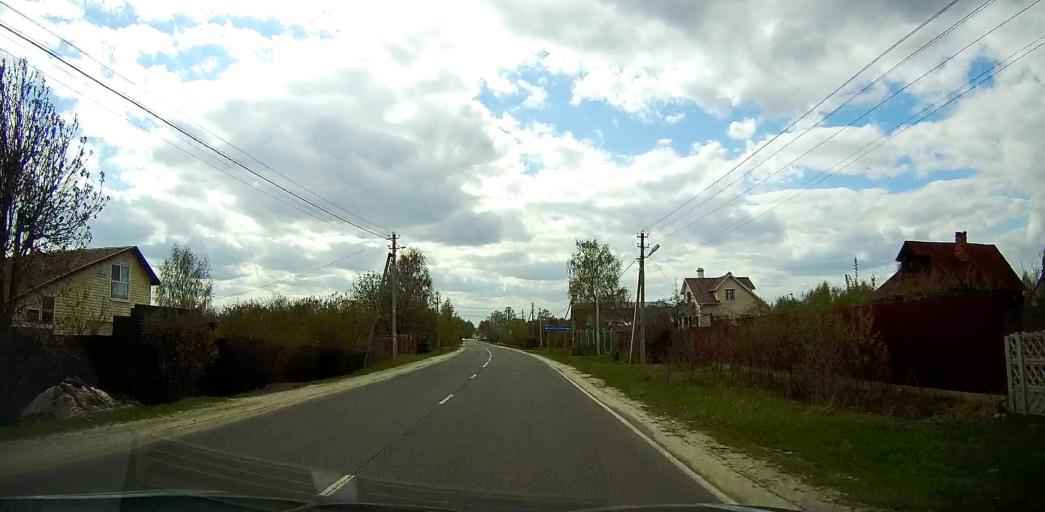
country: RU
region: Moskovskaya
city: Davydovo
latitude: 55.6302
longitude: 38.7400
